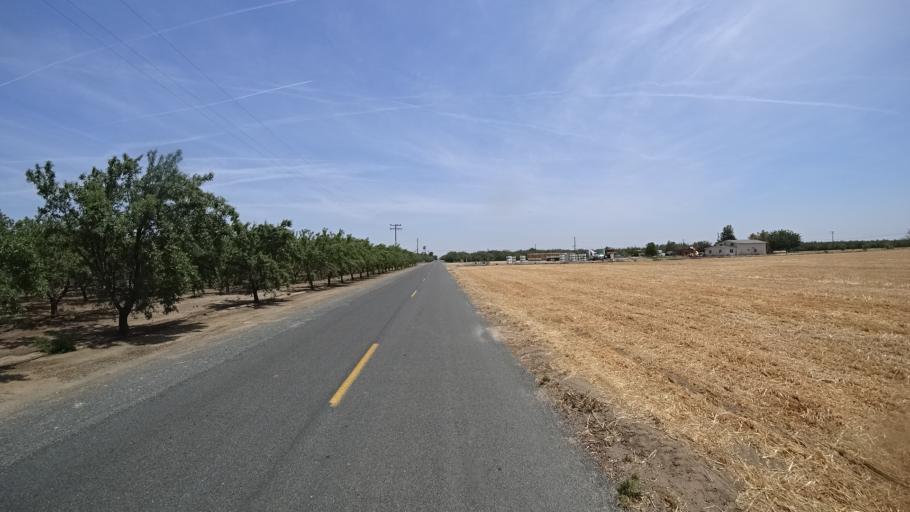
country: US
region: California
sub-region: Fresno County
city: Riverdale
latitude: 36.3947
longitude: -119.8713
